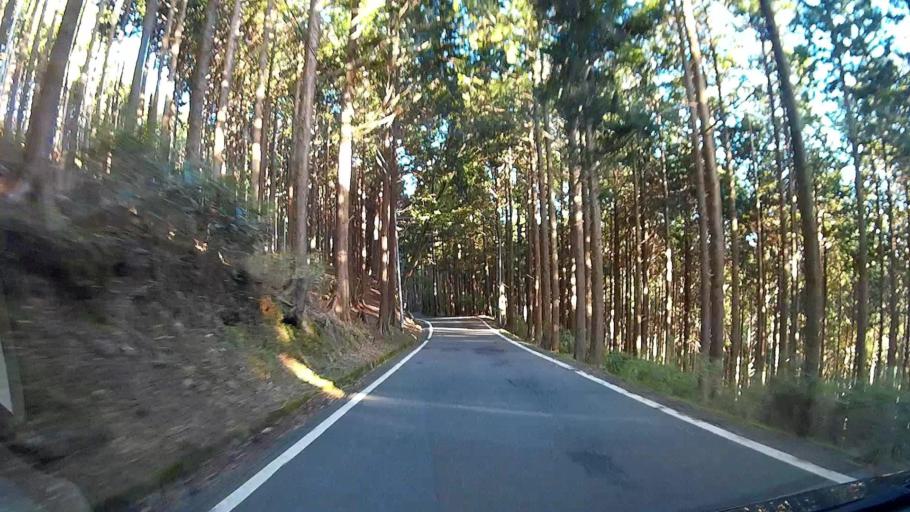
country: JP
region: Shizuoka
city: Shizuoka-shi
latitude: 35.1652
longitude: 138.2637
